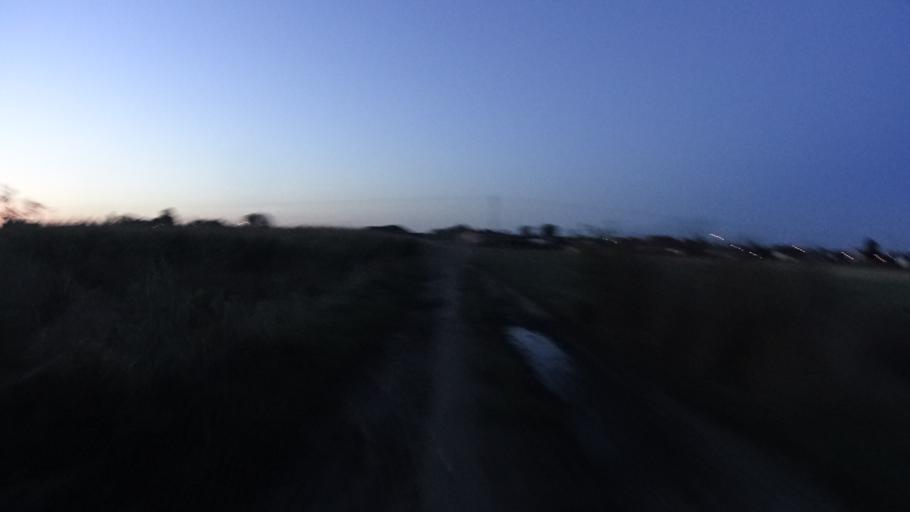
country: PL
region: Masovian Voivodeship
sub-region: Powiat warszawski zachodni
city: Ozarow Mazowiecki
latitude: 52.2277
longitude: 20.7904
